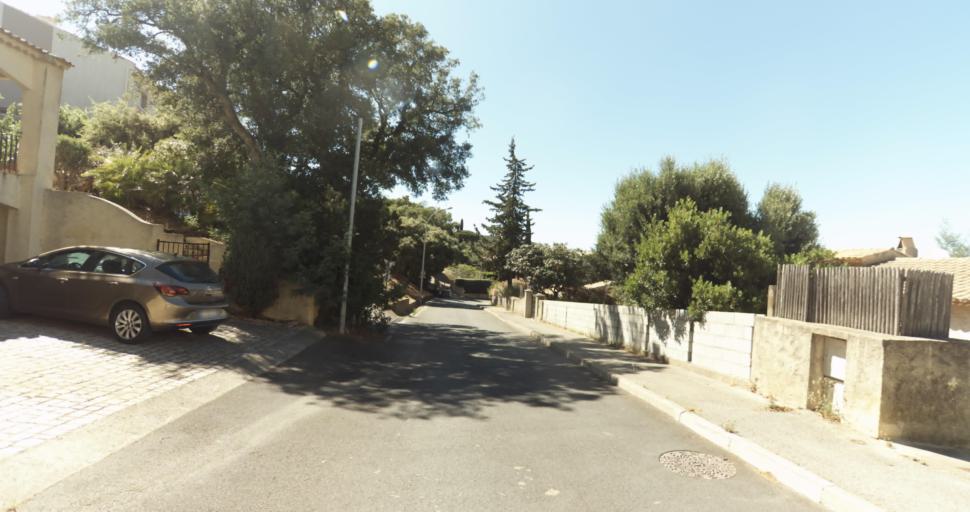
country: FR
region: Provence-Alpes-Cote d'Azur
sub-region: Departement du Var
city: La Croix-Valmer
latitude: 43.2098
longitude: 6.5666
